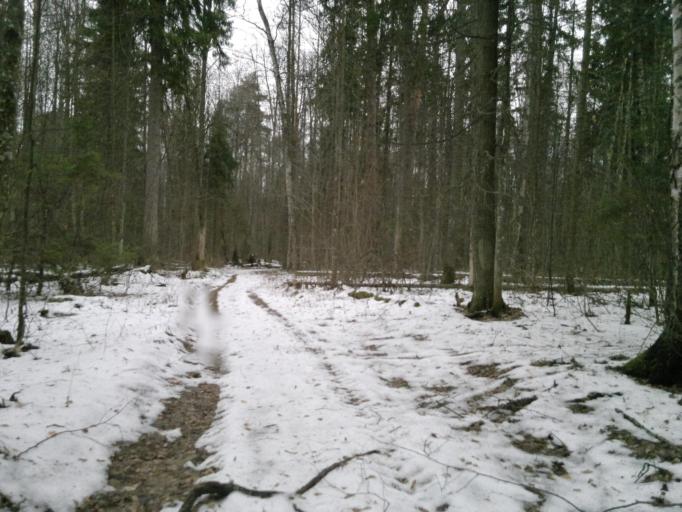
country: RU
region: Mariy-El
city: Yoshkar-Ola
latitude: 56.6058
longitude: 47.9545
